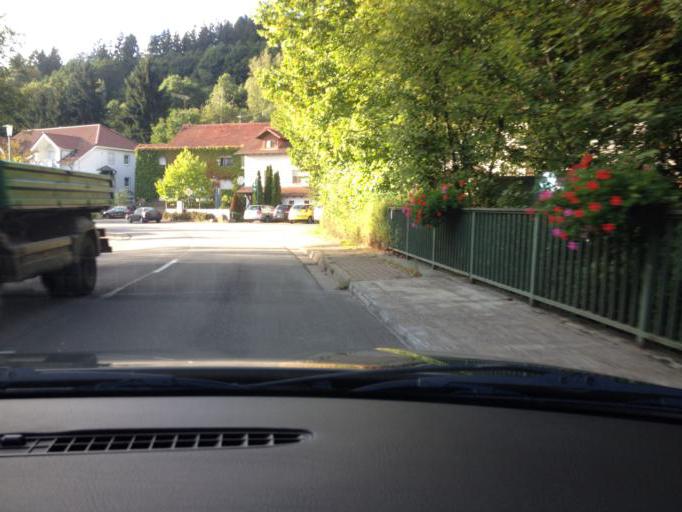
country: DE
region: Saarland
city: Marpingen
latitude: 49.4338
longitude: 7.0363
